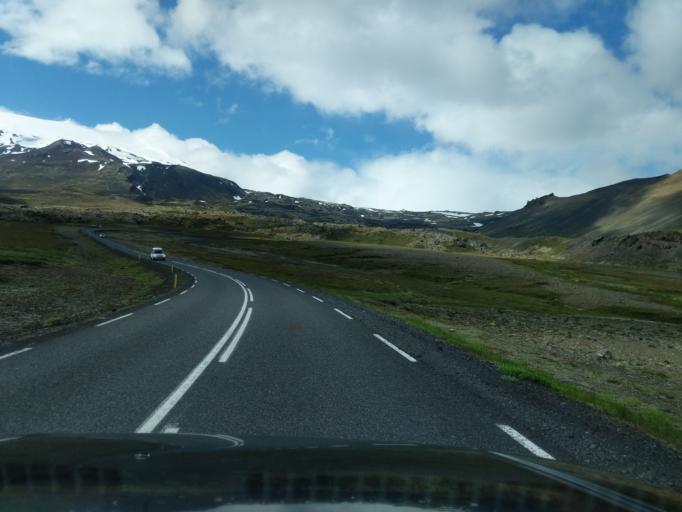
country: IS
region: West
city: Olafsvik
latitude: 64.7591
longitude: -23.6710
